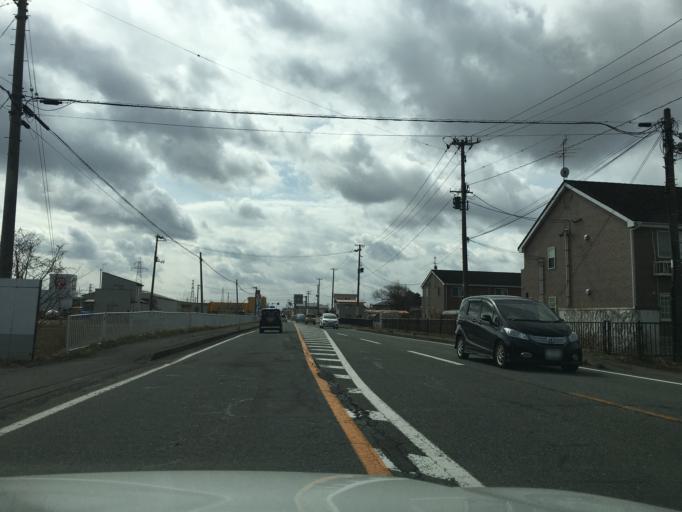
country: JP
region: Akita
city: Tenno
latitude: 39.9487
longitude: 140.0834
